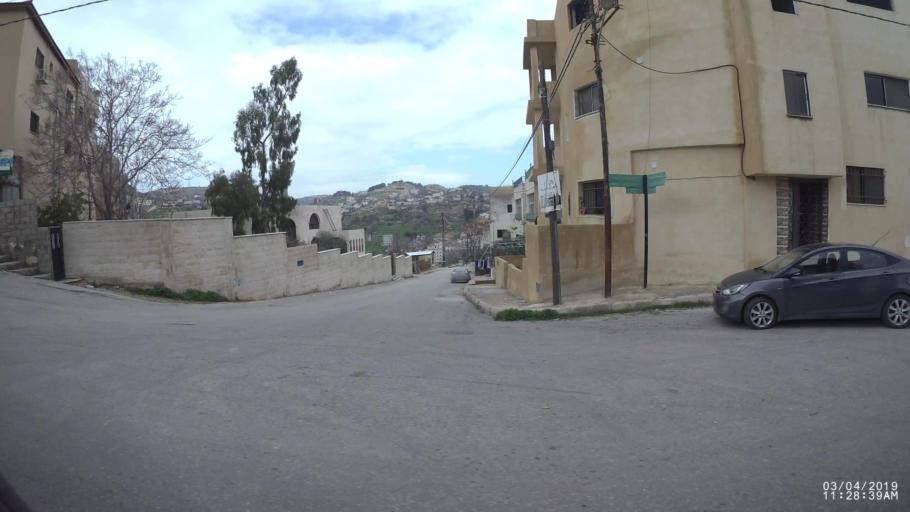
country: JO
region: Amman
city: Wadi as Sir
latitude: 31.9551
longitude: 35.8196
